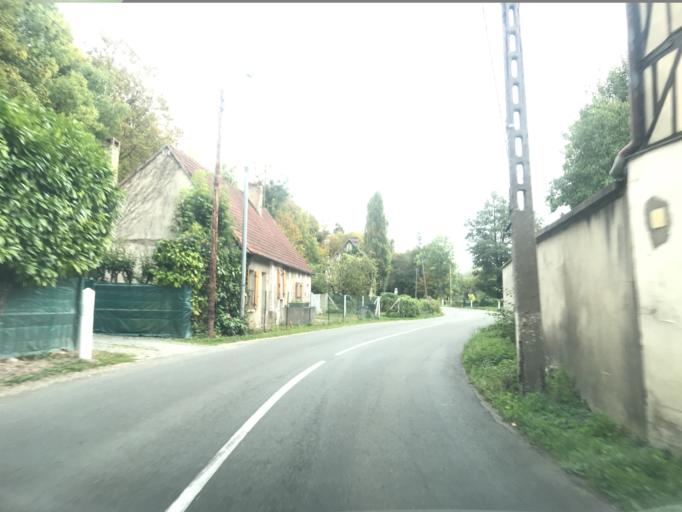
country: FR
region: Haute-Normandie
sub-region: Departement de l'Eure
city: Acquigny
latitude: 49.1650
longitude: 1.1919
